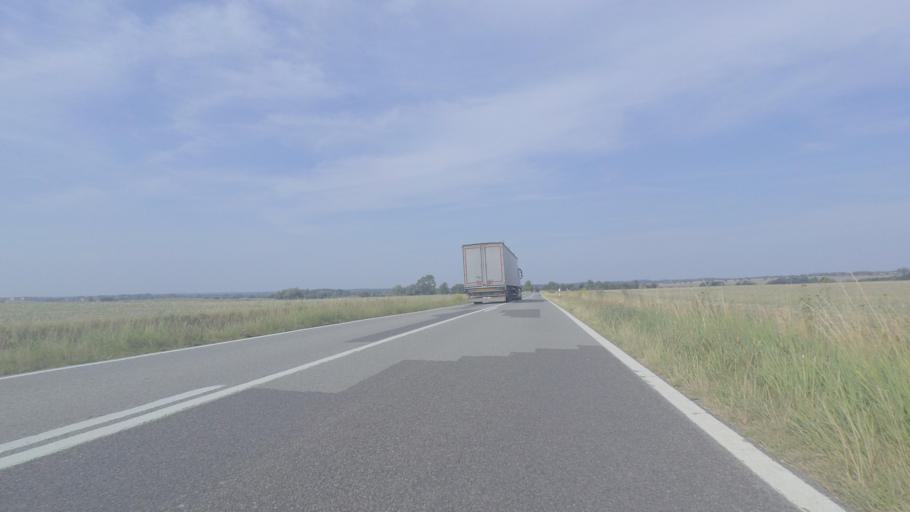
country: DE
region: Mecklenburg-Vorpommern
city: Gielow
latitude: 53.6522
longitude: 12.8116
